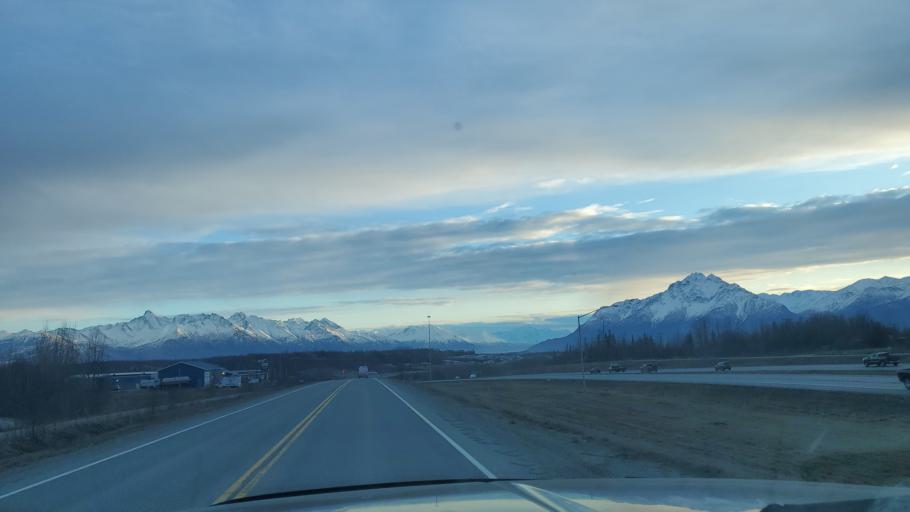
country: US
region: Alaska
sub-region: Matanuska-Susitna Borough
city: Lakes
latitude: 61.5693
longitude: -149.3355
